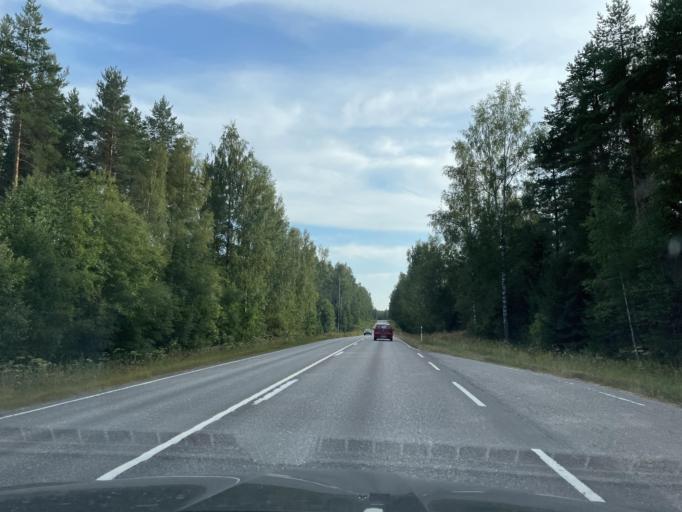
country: FI
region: Central Finland
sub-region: Jaemsae
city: Kuhmoinen
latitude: 61.5214
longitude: 25.1484
